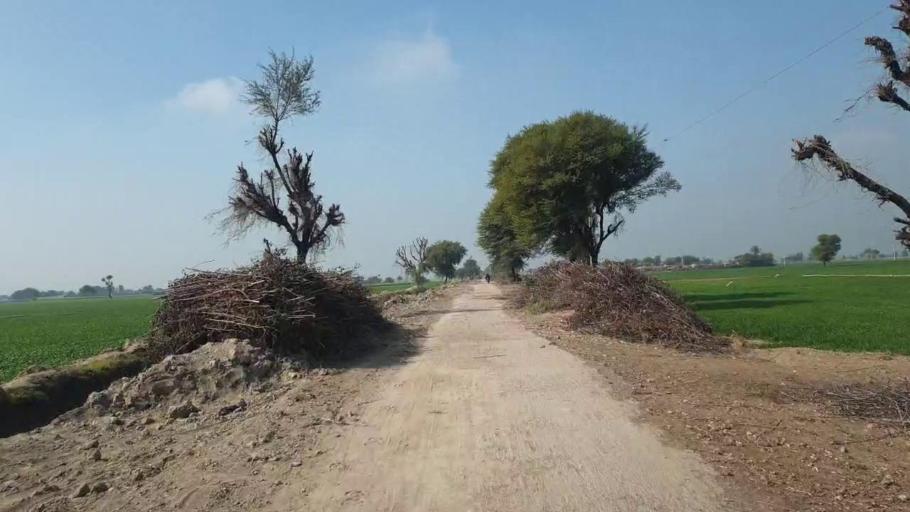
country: PK
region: Sindh
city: Shahdadpur
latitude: 26.0238
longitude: 68.5816
